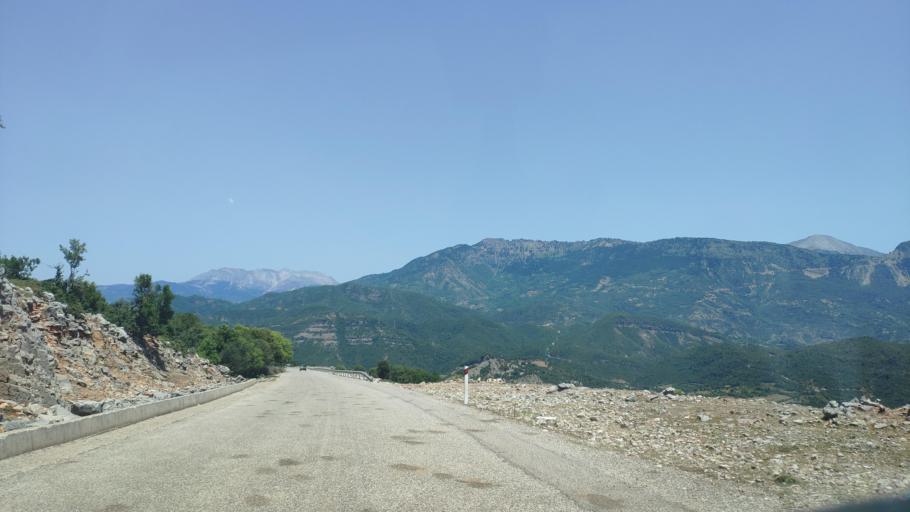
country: GR
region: Thessaly
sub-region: Nomos Kardhitsas
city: Anthiro
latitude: 39.1460
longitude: 21.3871
